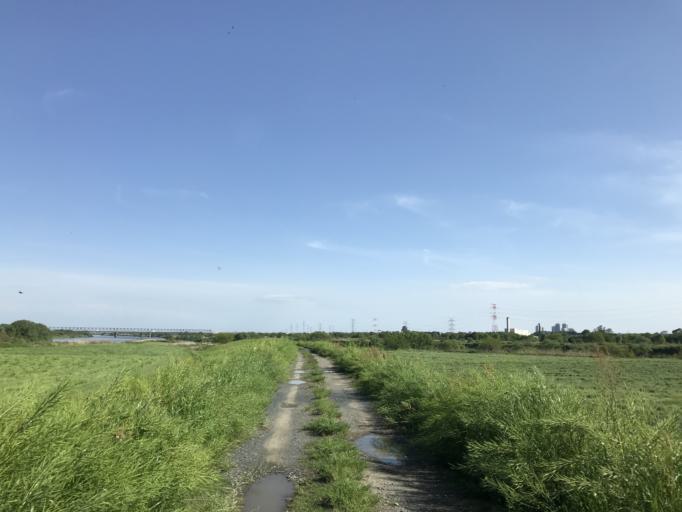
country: JP
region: Ibaraki
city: Moriya
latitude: 35.9418
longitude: 139.9443
